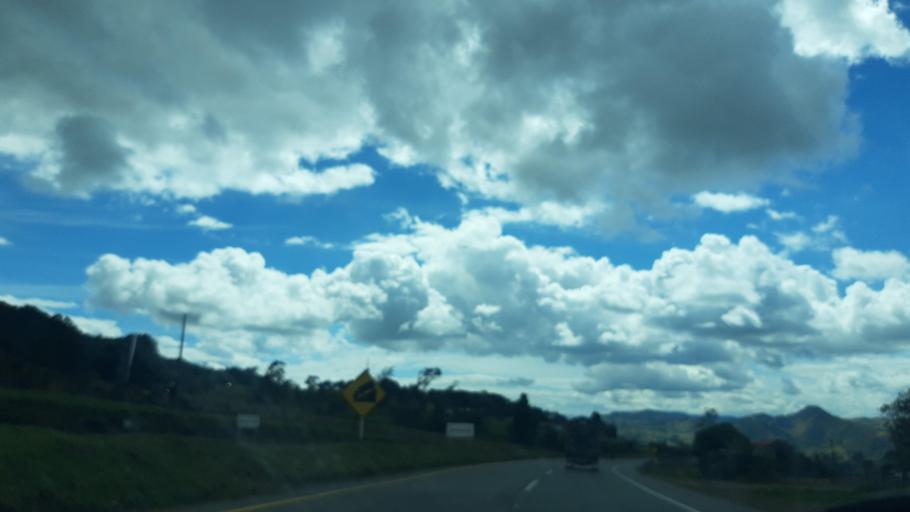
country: CO
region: Boyaca
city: Ventaquemada
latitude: 5.3446
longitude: -73.5514
